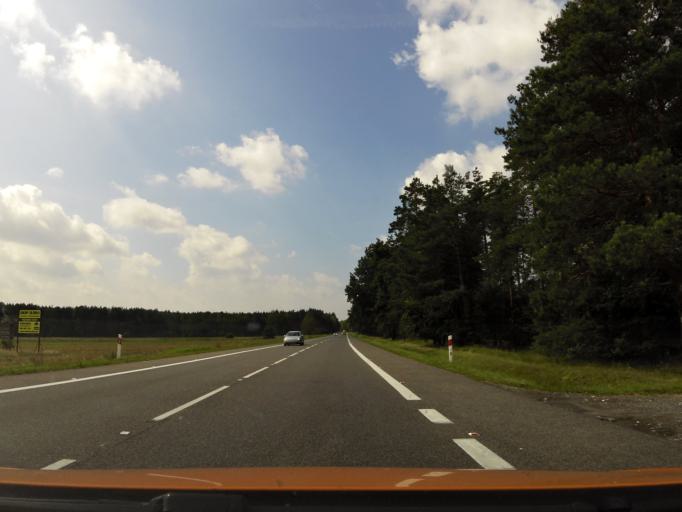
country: PL
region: West Pomeranian Voivodeship
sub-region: Powiat goleniowski
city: Mosty
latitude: 53.6076
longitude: 14.9039
